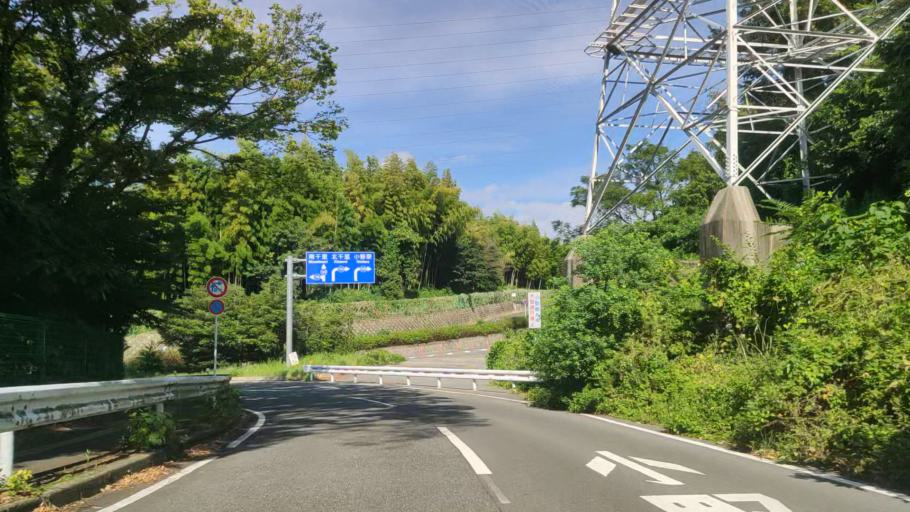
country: JP
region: Osaka
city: Suita
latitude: 34.8098
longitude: 135.5185
